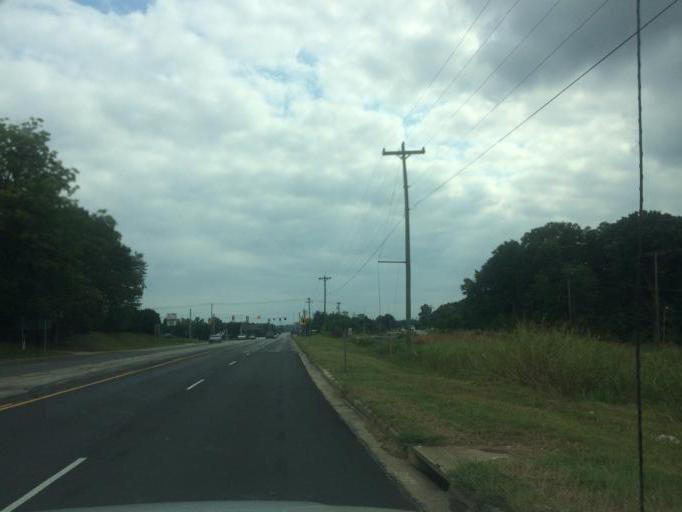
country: US
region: South Carolina
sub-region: Greenville County
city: Gantt
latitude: 34.7904
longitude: -82.4248
